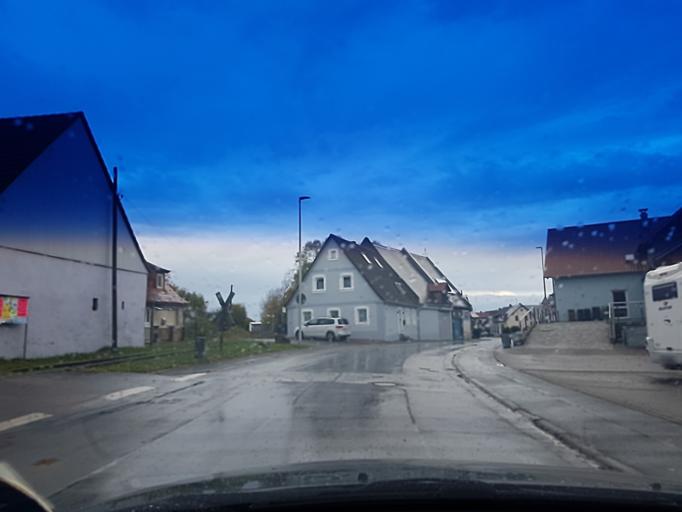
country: DE
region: Bavaria
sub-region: Regierungsbezirk Mittelfranken
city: Muhlhausen
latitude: 49.7552
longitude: 10.7768
